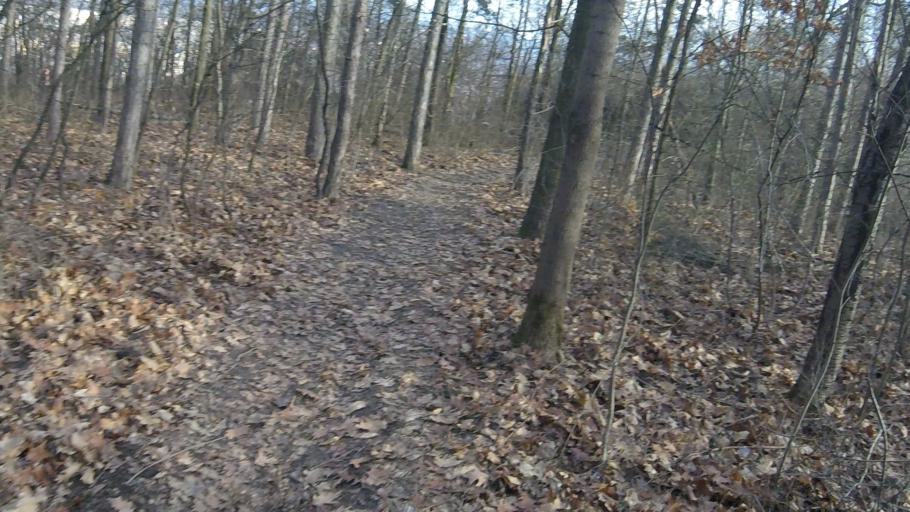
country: HU
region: Pest
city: Urom
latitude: 47.5950
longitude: 19.0350
